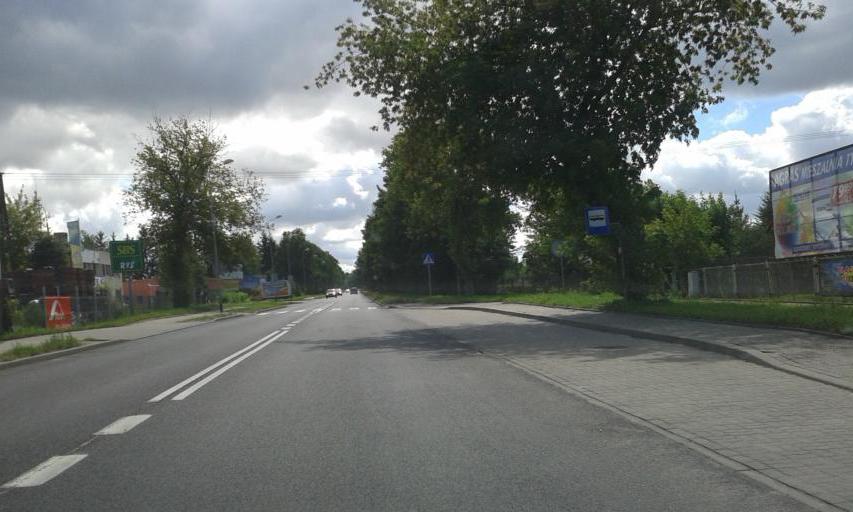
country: PL
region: West Pomeranian Voivodeship
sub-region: Powiat walecki
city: Walcz
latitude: 53.2629
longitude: 16.4932
